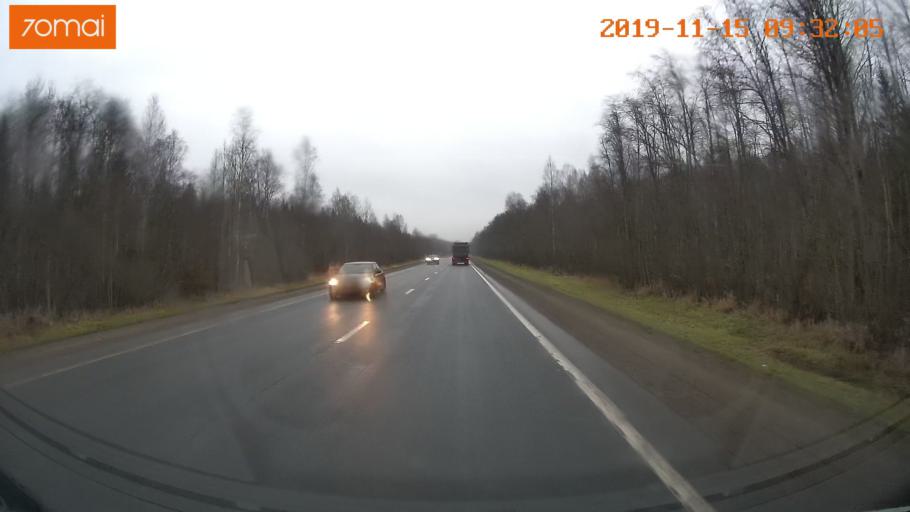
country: RU
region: Vologda
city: Sheksna
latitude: 59.2730
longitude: 38.3261
